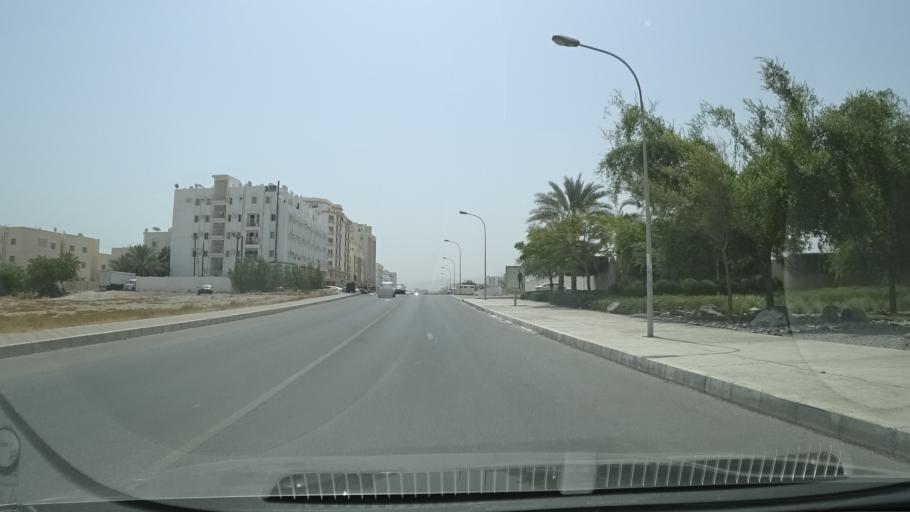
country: OM
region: Muhafazat Masqat
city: Bawshar
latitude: 23.5932
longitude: 58.3685
